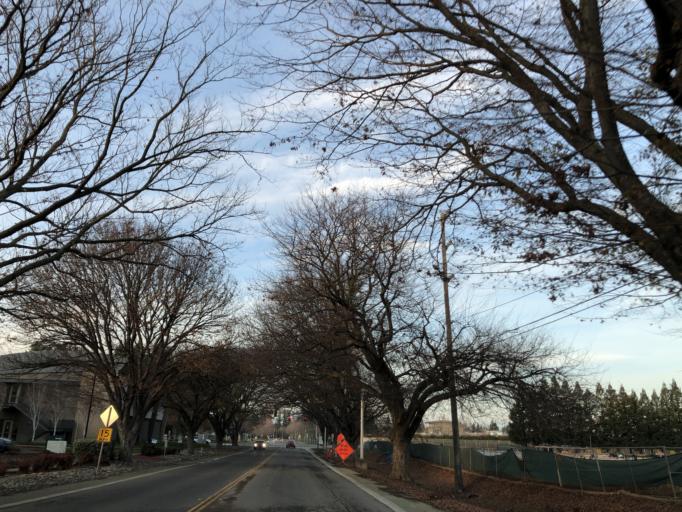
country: US
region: California
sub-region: Sacramento County
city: Rosemont
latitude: 38.5528
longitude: -121.4185
